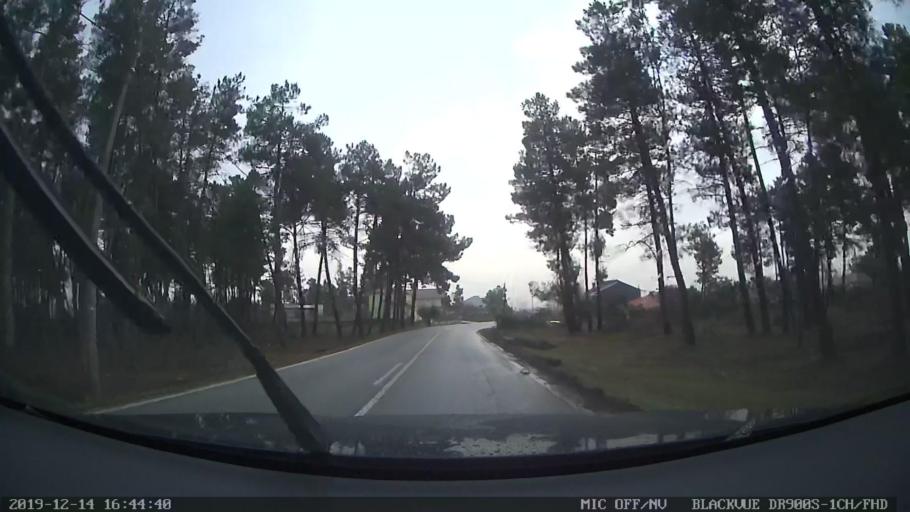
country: PT
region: Vila Real
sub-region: Murca
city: Murca
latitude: 41.3938
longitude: -7.4938
